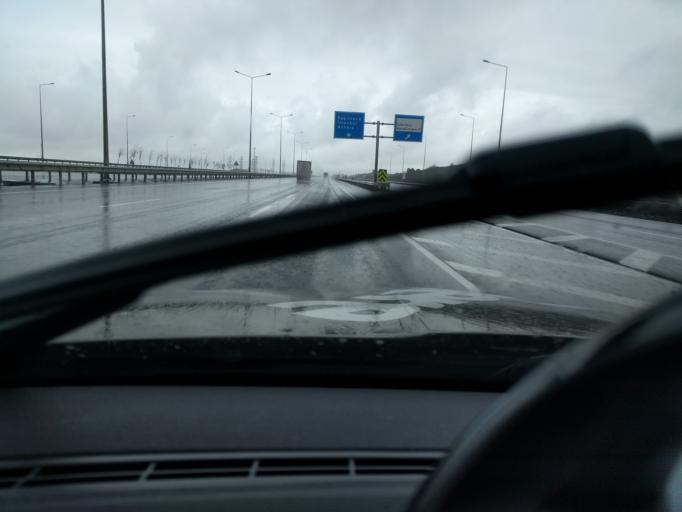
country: TR
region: Istanbul
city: Durusu
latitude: 41.2460
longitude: 28.7322
